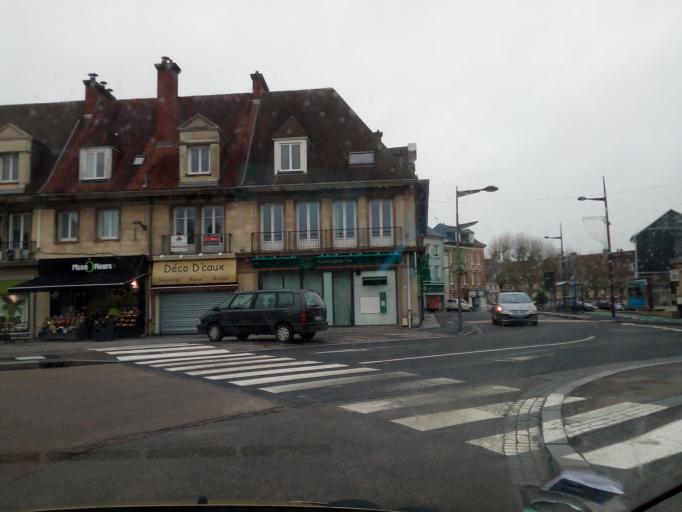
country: FR
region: Haute-Normandie
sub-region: Departement de la Seine-Maritime
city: Yvetot
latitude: 49.6168
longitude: 0.7552
